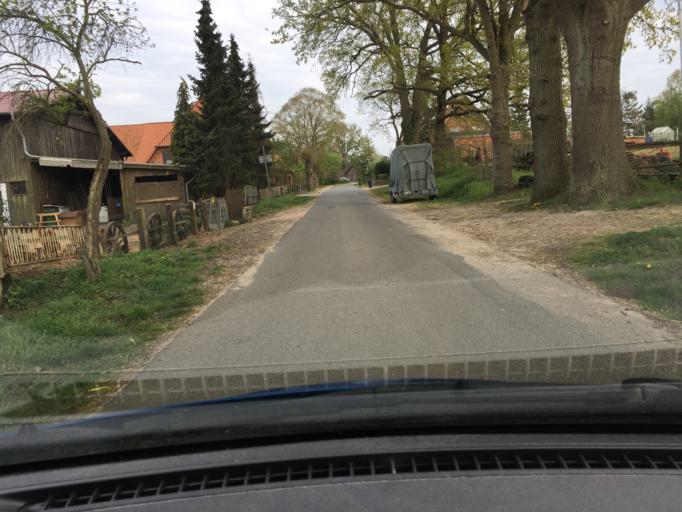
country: DE
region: Lower Saxony
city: Neetze
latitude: 53.2690
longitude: 10.6155
